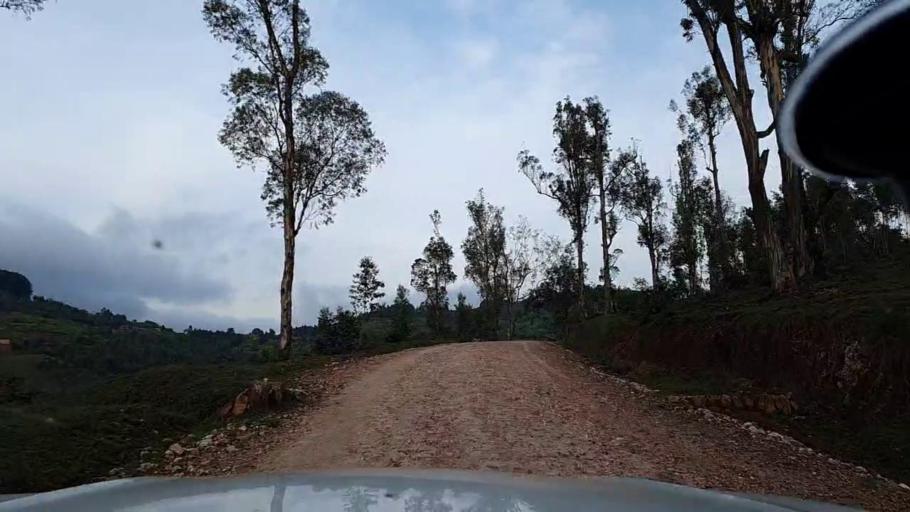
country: RW
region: Southern Province
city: Nyanza
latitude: -2.2113
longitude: 29.6267
